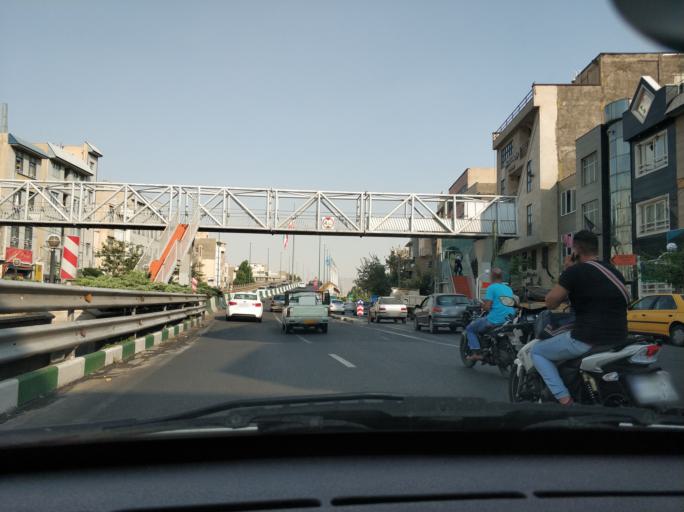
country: IR
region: Tehran
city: Tehran
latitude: 35.7260
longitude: 51.4696
